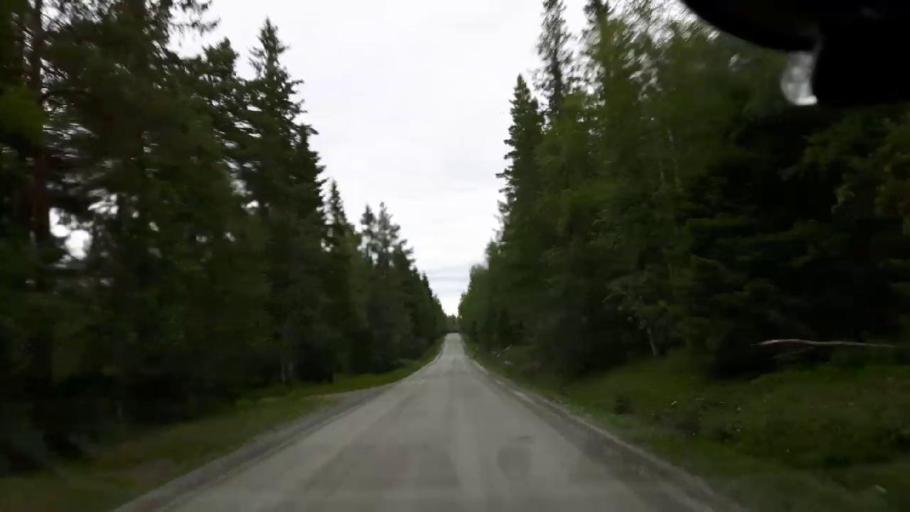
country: SE
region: Jaemtland
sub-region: OEstersunds Kommun
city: Brunflo
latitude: 63.0915
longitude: 15.1653
